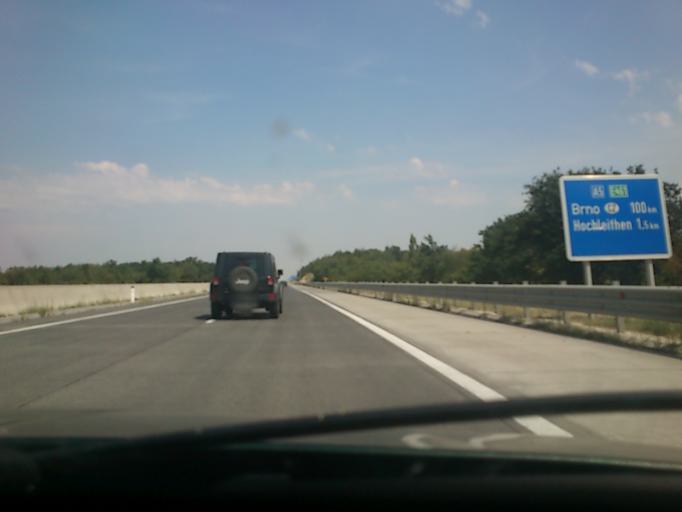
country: AT
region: Lower Austria
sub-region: Politischer Bezirk Mistelbach
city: Wolkersdorf im Weinviertel
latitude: 48.4087
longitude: 16.5363
